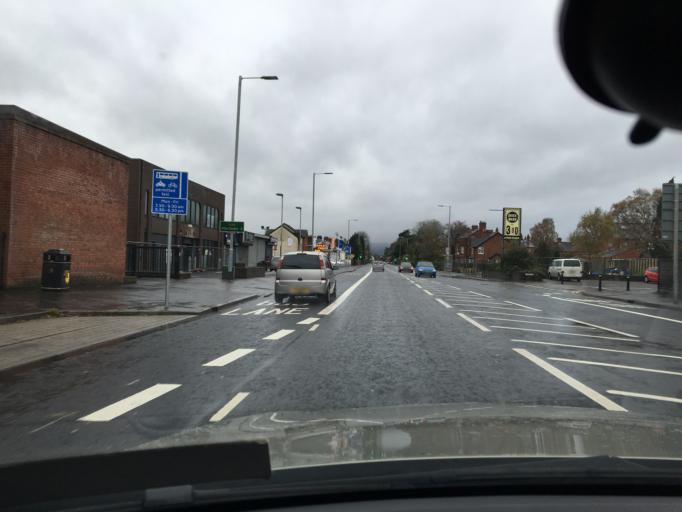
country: GB
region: Northern Ireland
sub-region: Castlereagh District
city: Castlereagh
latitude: 54.5947
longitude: -5.8560
